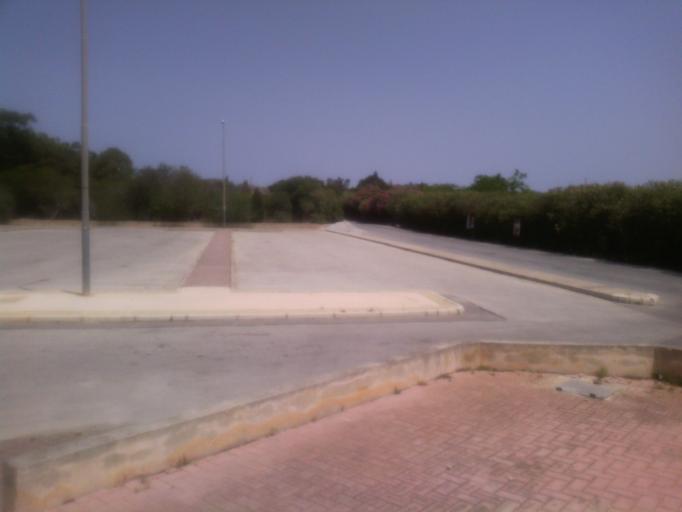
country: MT
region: L-Imdina
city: Imdina
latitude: 35.8895
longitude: 14.4191
